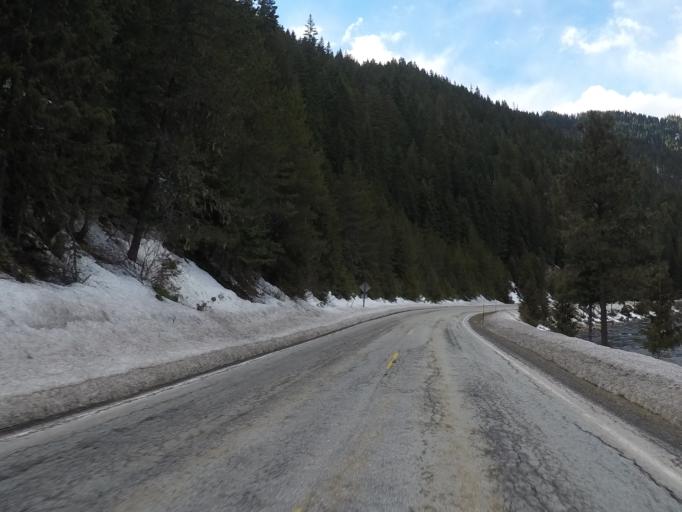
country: US
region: Montana
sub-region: Mineral County
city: Superior
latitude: 46.4817
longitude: -114.8772
